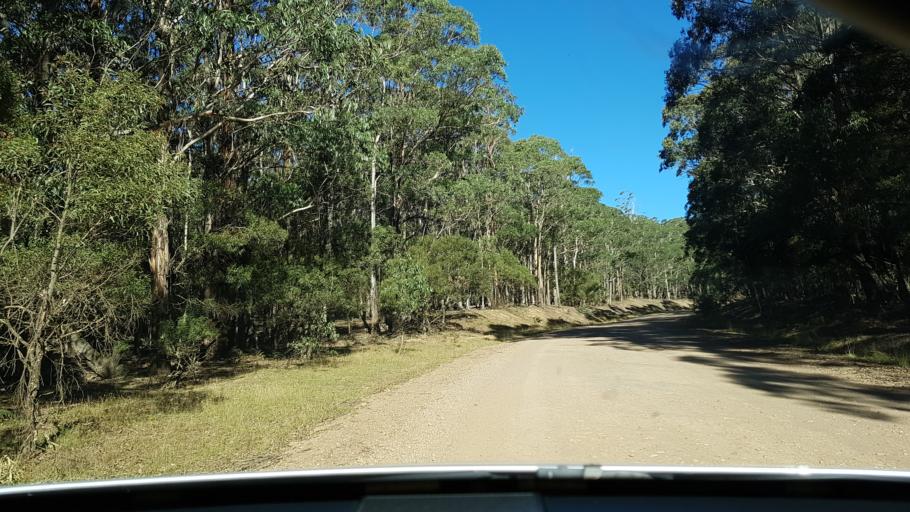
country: AU
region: New South Wales
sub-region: Oberon
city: Oberon
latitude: -33.8346
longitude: 150.0125
